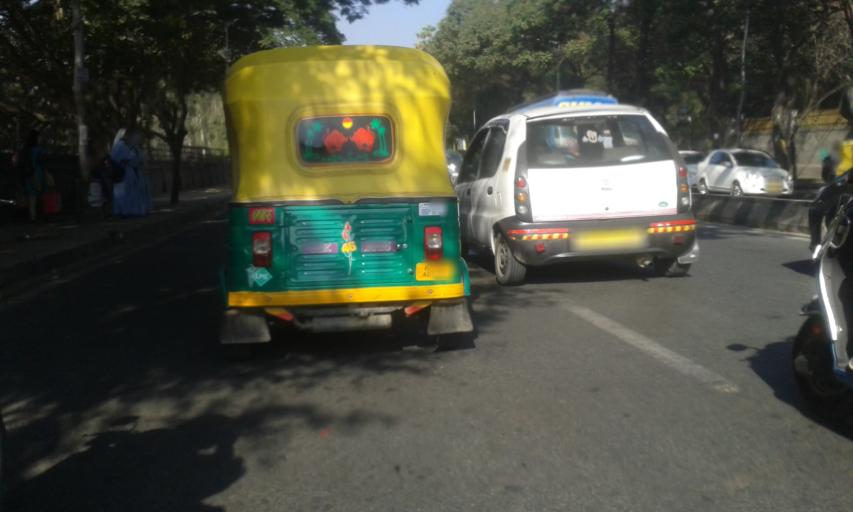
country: IN
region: Karnataka
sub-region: Bangalore Urban
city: Bangalore
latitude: 12.9288
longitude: 77.6174
